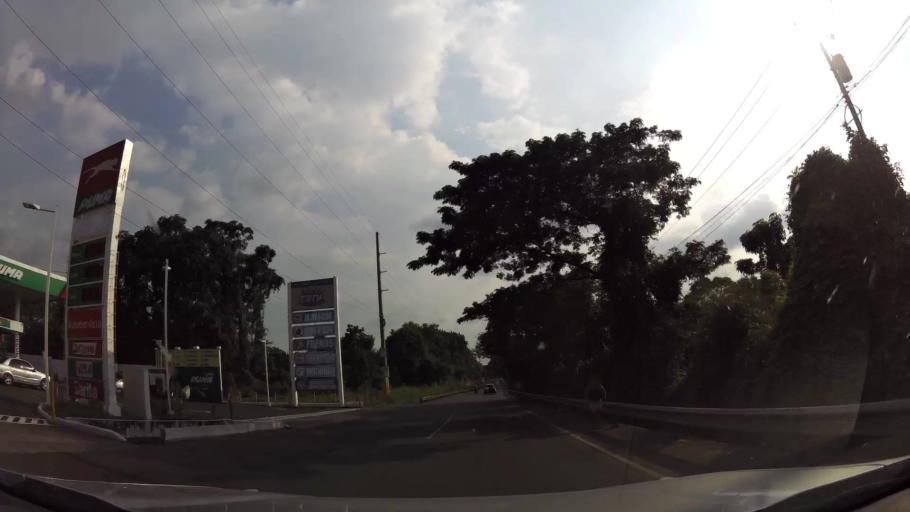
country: GT
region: Escuintla
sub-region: Municipio de Escuintla
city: Escuintla
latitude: 14.3102
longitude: -90.7928
